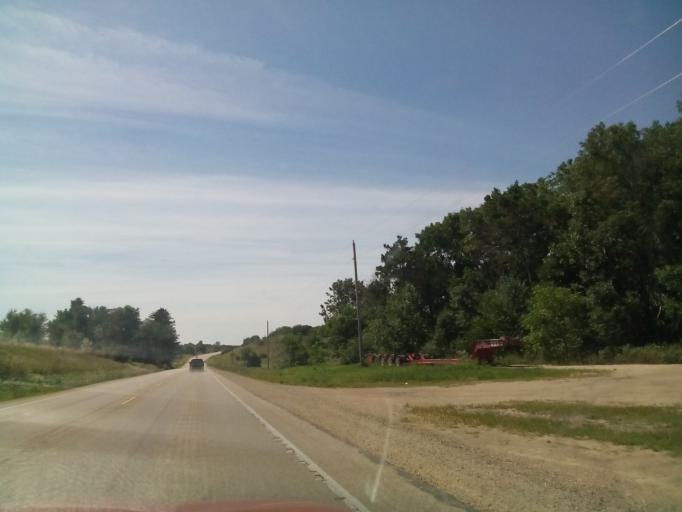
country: US
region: Wisconsin
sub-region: Green County
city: Monroe
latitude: 42.6389
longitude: -89.6316
